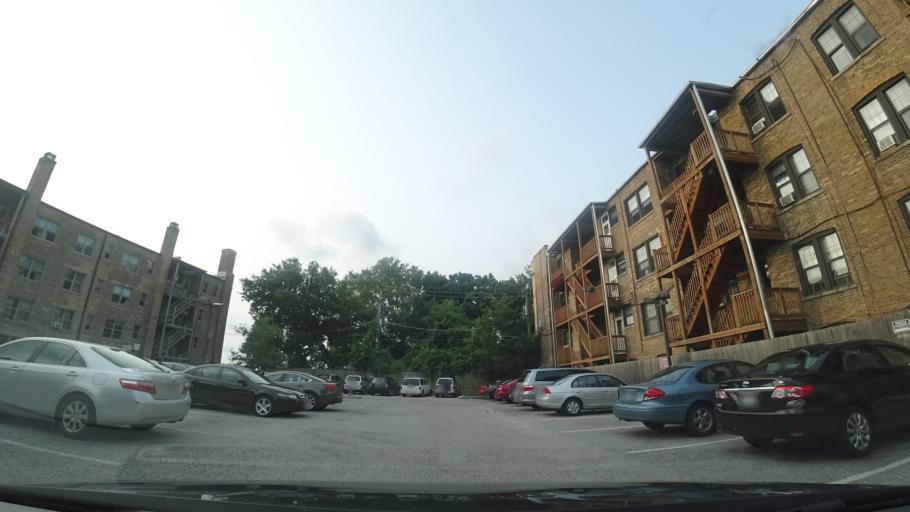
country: US
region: Illinois
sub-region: Cook County
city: Evanston
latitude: 42.0138
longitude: -87.6627
